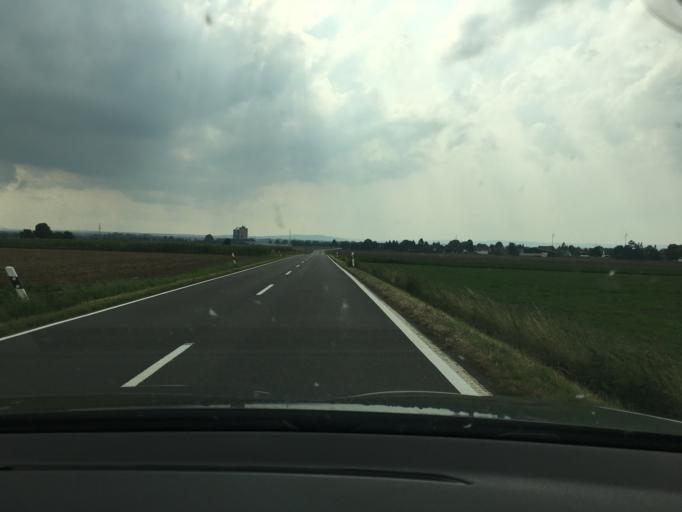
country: DE
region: North Rhine-Westphalia
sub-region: Regierungsbezirk Koln
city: Merzenich
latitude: 50.7862
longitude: 6.5612
